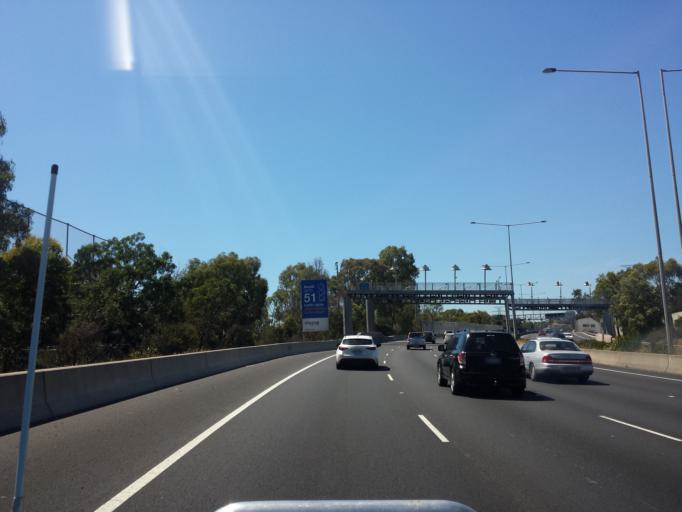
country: AU
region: Victoria
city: Toorak
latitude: -37.8316
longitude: 145.0221
